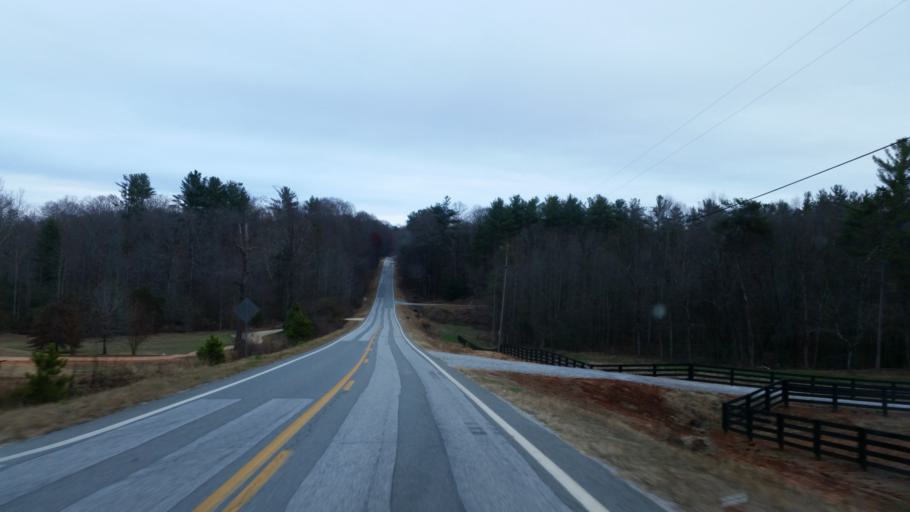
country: US
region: Georgia
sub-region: Dawson County
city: Dawsonville
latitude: 34.4960
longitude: -84.1982
